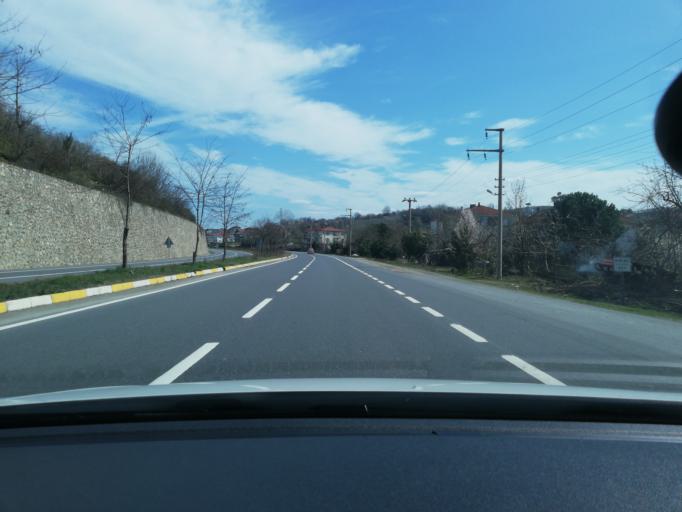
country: TR
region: Duzce
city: Akcakoca
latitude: 41.0964
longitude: 31.2169
